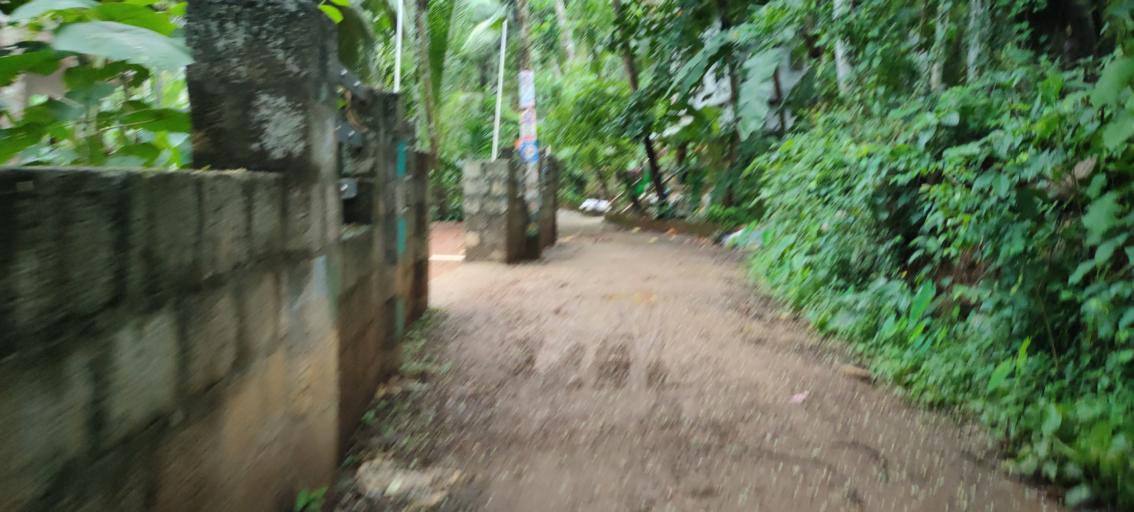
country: IN
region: Kerala
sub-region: Malappuram
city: Ponnani
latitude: 10.7674
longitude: 76.0346
